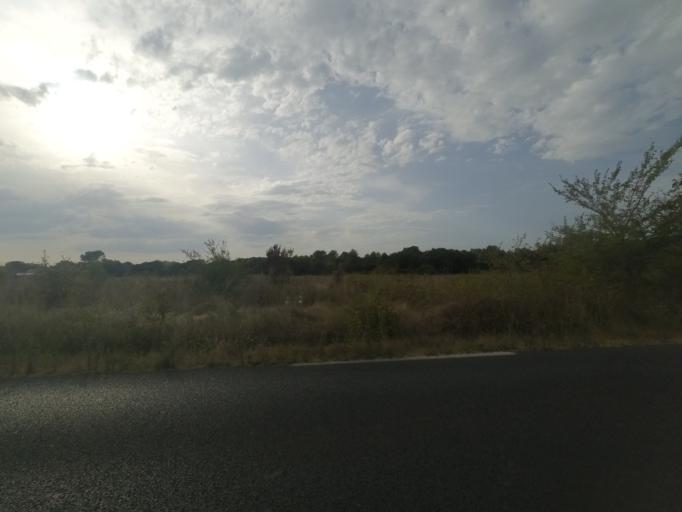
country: FR
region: Languedoc-Roussillon
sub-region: Departement de l'Herault
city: Castries
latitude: 43.6863
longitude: 3.9958
